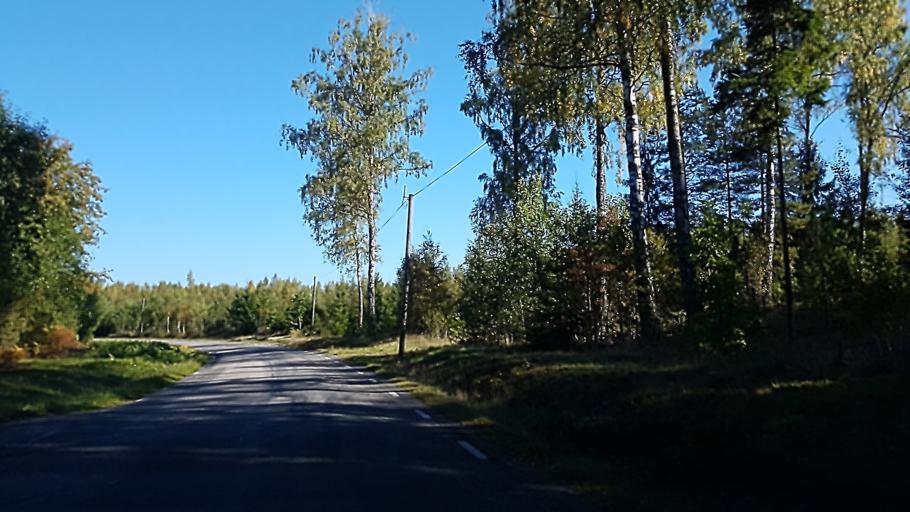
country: SE
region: Kronoberg
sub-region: Ljungby Kommun
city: Ljungby
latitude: 56.8035
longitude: 14.0338
